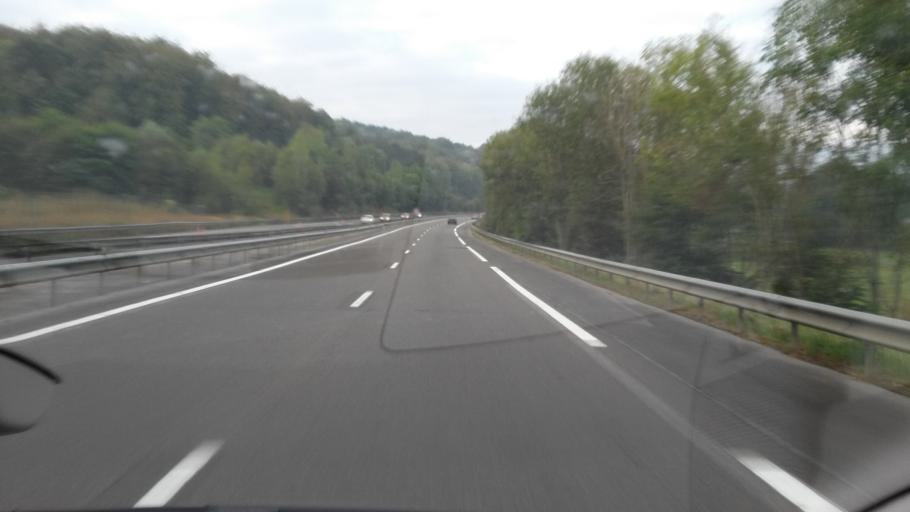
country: FR
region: Champagne-Ardenne
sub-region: Departement des Ardennes
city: La Francheville
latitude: 49.6738
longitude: 4.6541
